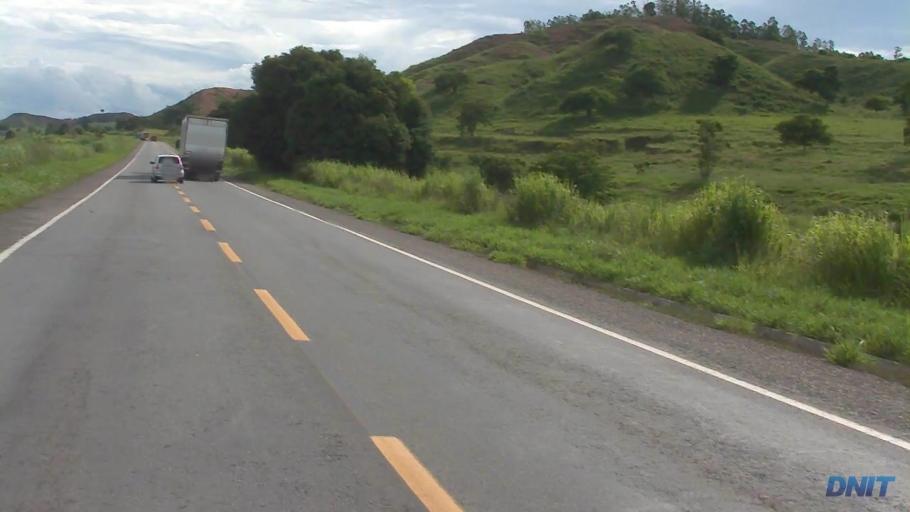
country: BR
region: Minas Gerais
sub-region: Belo Oriente
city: Belo Oriente
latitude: -19.1883
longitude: -42.2691
